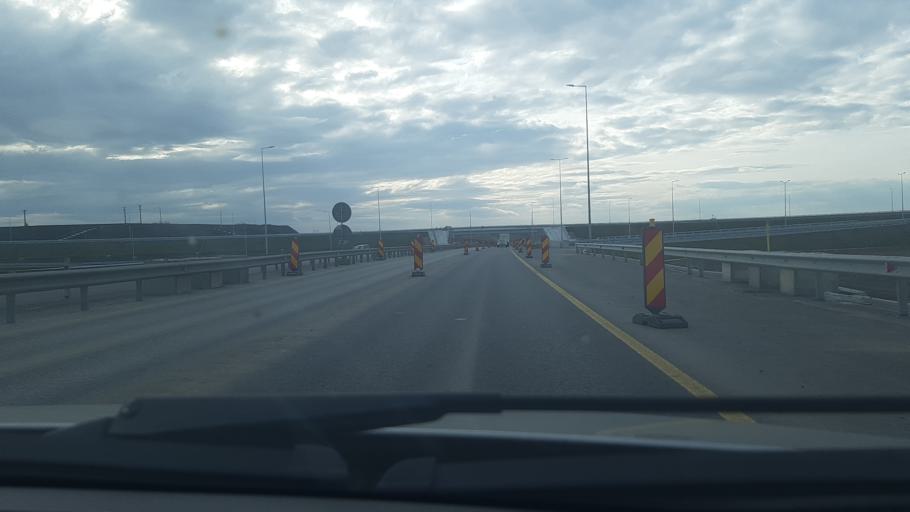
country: RO
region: Mures
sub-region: Comuna Iernut
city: Cipau
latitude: 46.4311
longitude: 24.2721
